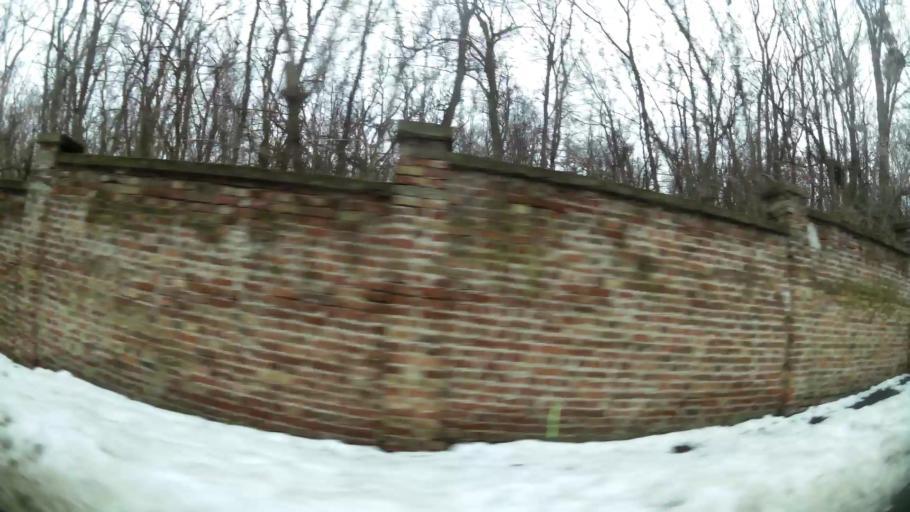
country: RS
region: Central Serbia
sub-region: Belgrade
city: Savski Venac
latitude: 44.7604
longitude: 20.4528
